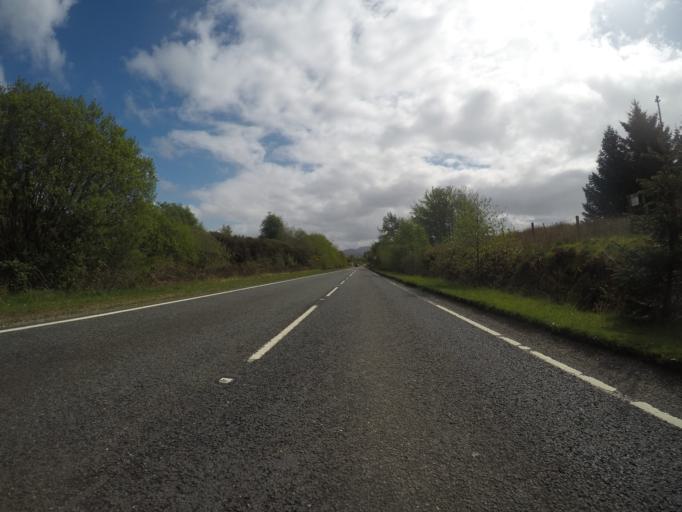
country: GB
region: Scotland
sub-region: Highland
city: Portree
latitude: 57.2445
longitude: -5.9203
